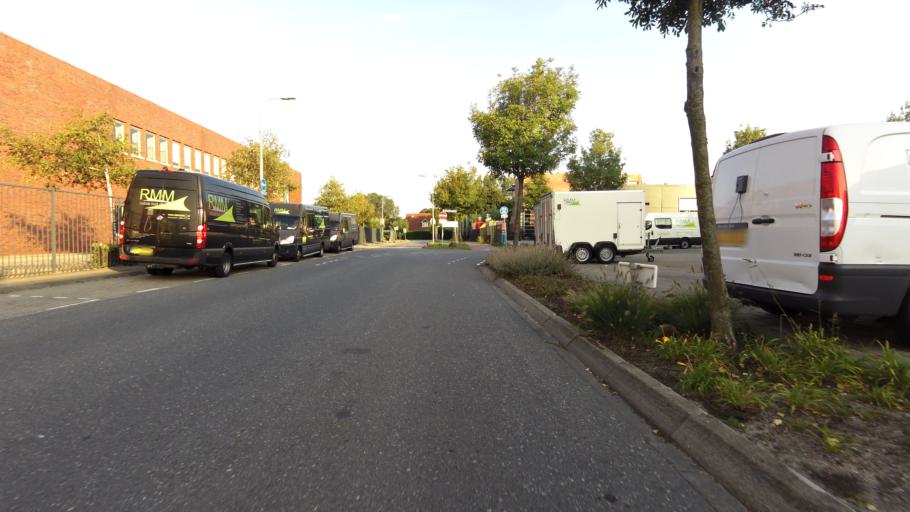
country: NL
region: South Holland
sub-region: Gemeente Teylingen
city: Voorhout
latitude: 52.2097
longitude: 4.4915
